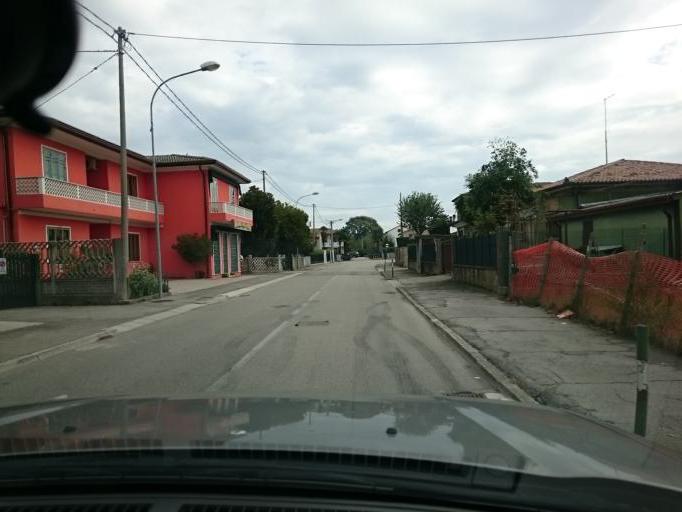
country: IT
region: Veneto
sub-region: Provincia di Padova
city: Vallonga
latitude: 45.2720
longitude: 12.0794
